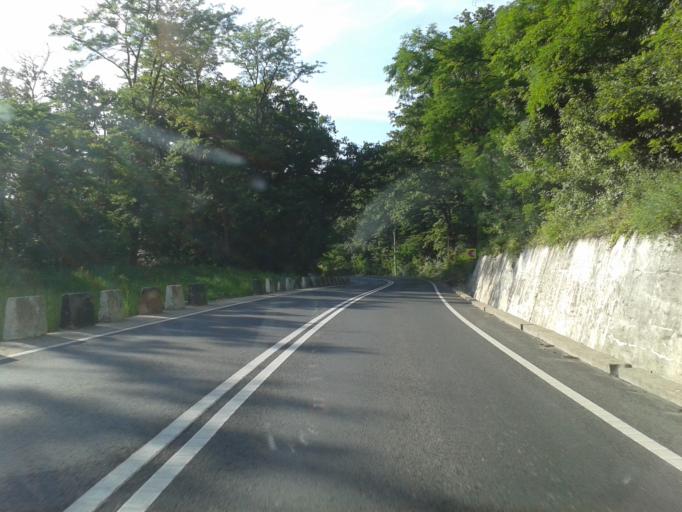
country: RO
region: Hunedoara
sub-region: Oras Hateg
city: Hateg
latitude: 45.6140
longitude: 22.9756
